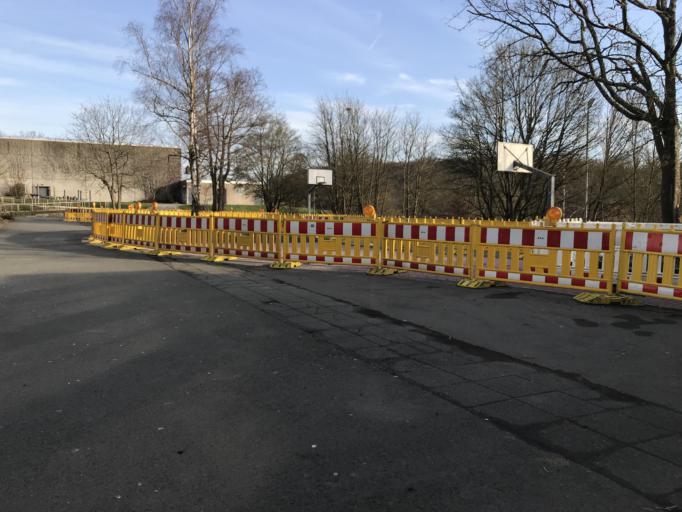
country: DE
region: Hesse
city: Weilburg
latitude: 50.4904
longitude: 8.2800
